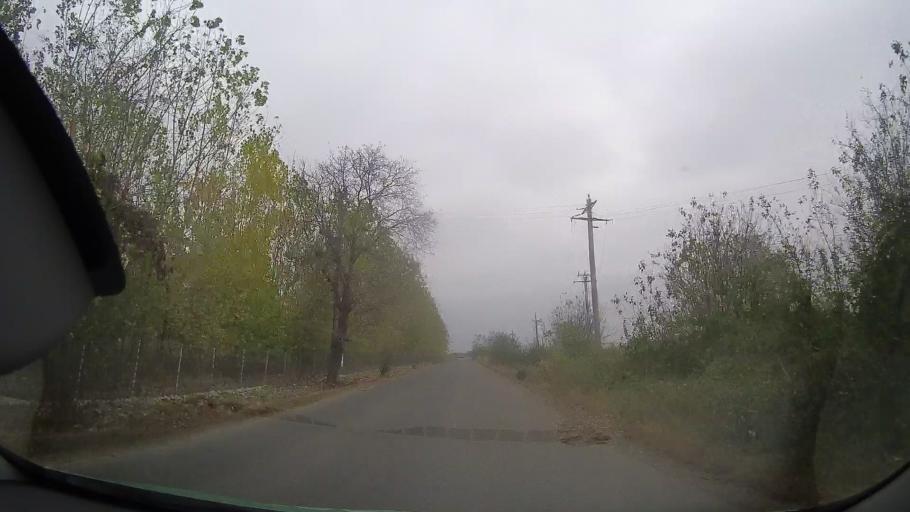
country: RO
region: Buzau
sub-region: Comuna Glodeanu-Silistea
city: Glodeanu-Silistea
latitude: 44.8178
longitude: 26.8406
